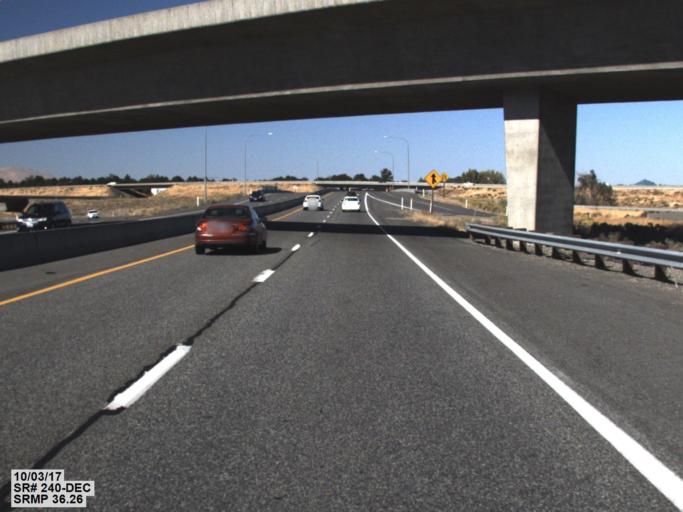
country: US
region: Washington
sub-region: Benton County
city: Richland
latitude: 46.2567
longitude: -119.2604
